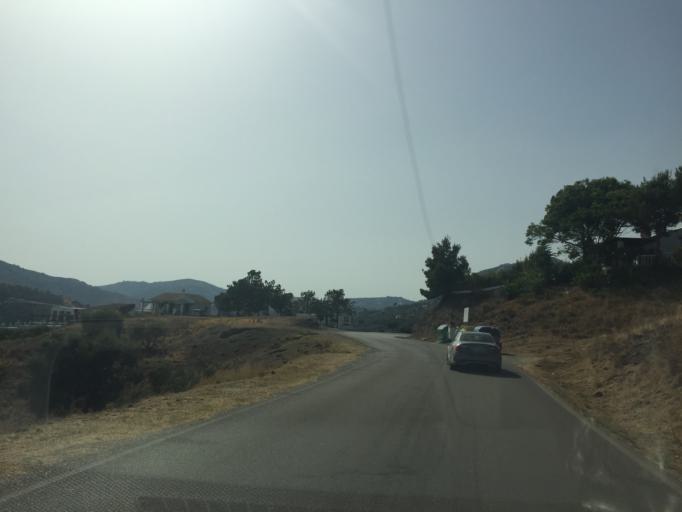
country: ES
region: Andalusia
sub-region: Provincia de Malaga
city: Frigiliana
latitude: 36.8025
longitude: -3.9189
